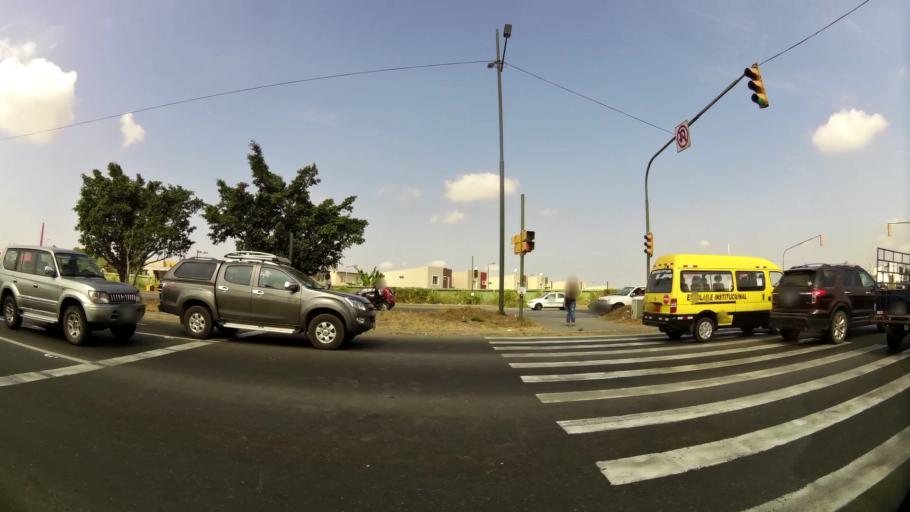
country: EC
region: Guayas
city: Eloy Alfaro
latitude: -2.1797
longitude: -79.8238
